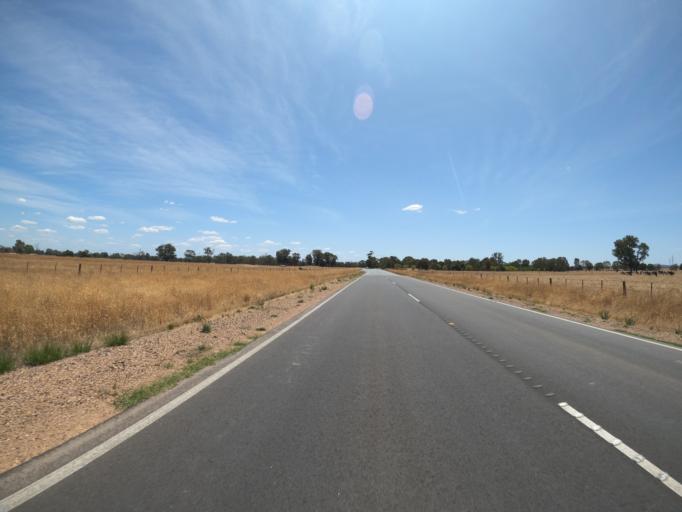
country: AU
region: Victoria
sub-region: Benalla
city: Benalla
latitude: -36.4998
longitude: 146.0215
